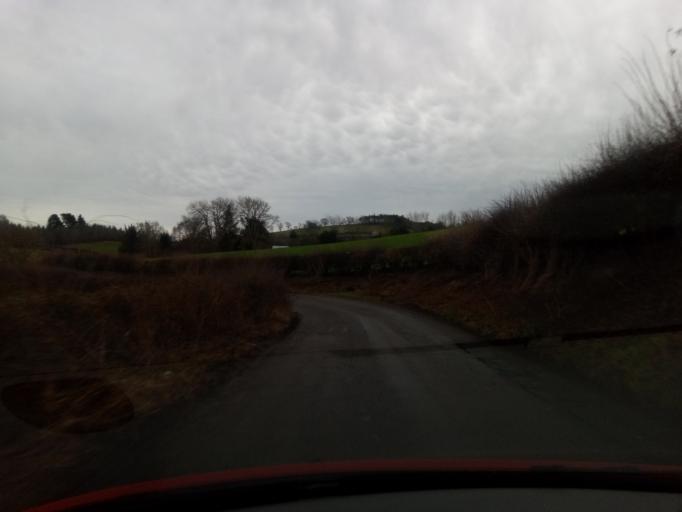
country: GB
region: England
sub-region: Northumberland
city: Wooler
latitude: 55.5497
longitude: -2.0274
